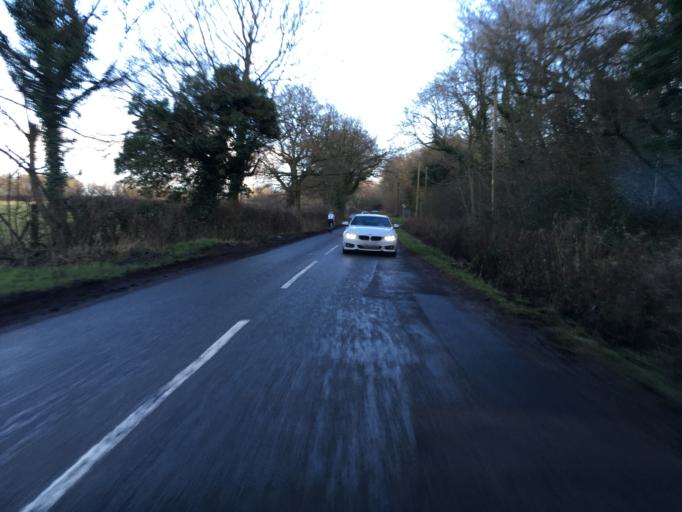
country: GB
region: England
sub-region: Warwickshire
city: Stratford-upon-Avon
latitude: 52.2436
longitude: -1.7282
